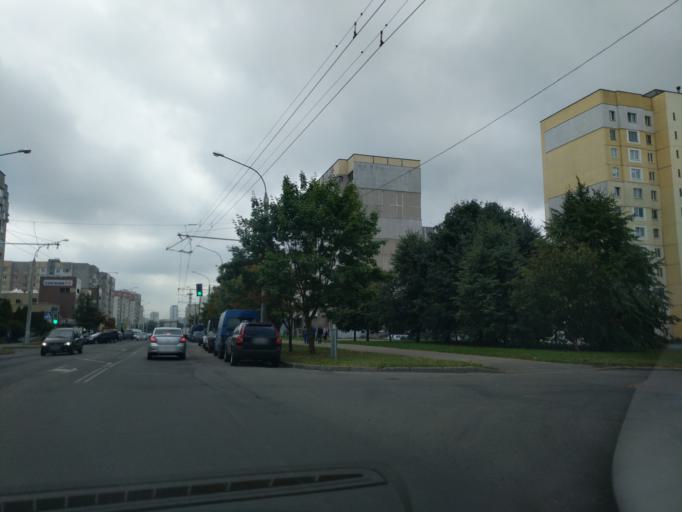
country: BY
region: Minsk
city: Novoye Medvezhino
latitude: 53.8852
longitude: 27.4379
